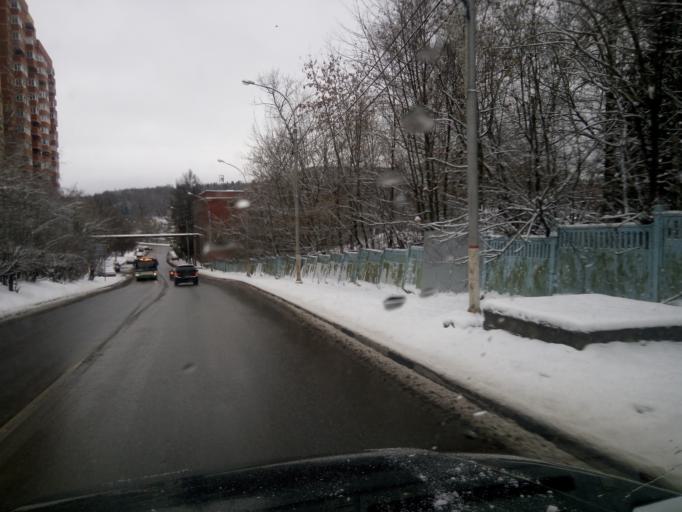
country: RU
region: Moskovskaya
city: Skhodnya
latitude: 55.9595
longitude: 37.3067
